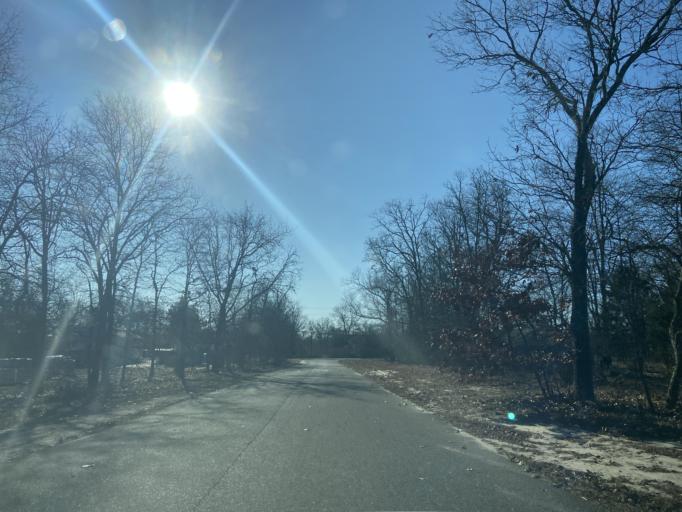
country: US
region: New Jersey
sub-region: Cumberland County
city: Vineland
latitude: 39.4965
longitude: -75.0672
